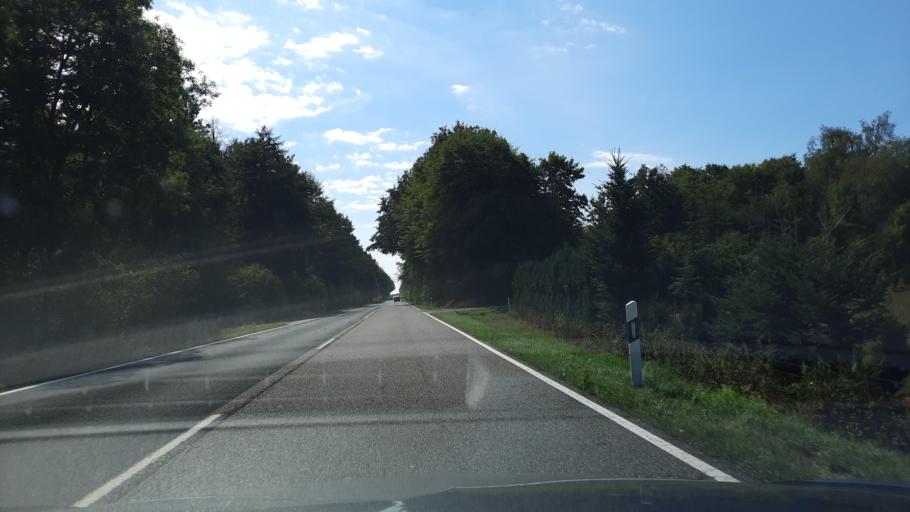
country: DE
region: Rheinland-Pfalz
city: Paschel
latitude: 49.6315
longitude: 6.6640
